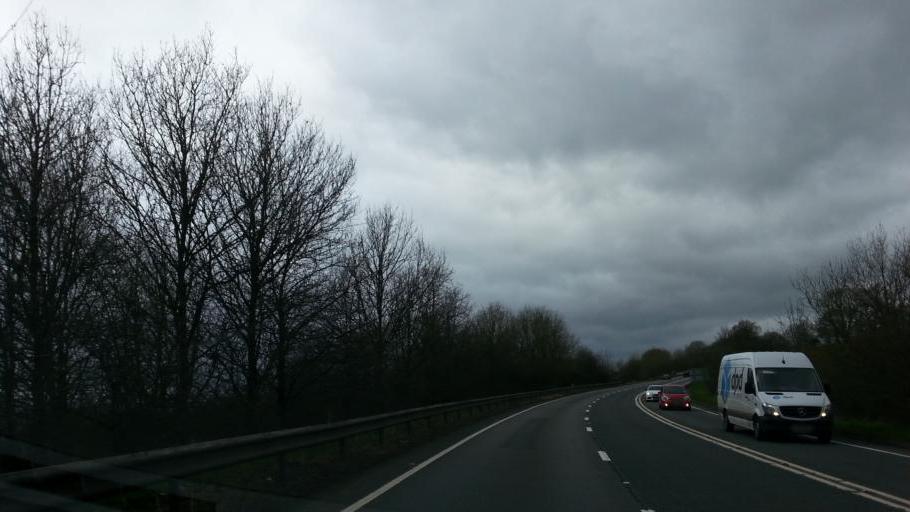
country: GB
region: England
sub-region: Devon
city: Tiverton
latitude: 50.9179
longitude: -3.5108
